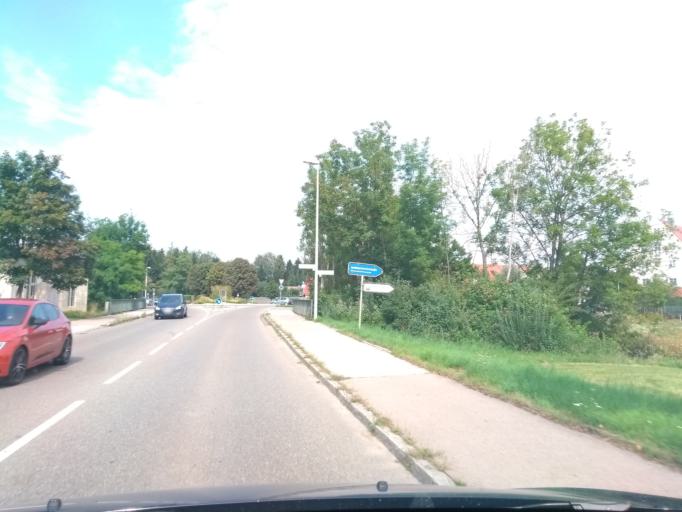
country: DE
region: Bavaria
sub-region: Upper Bavaria
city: Markt Indersdorf
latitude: 48.3573
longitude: 11.3806
